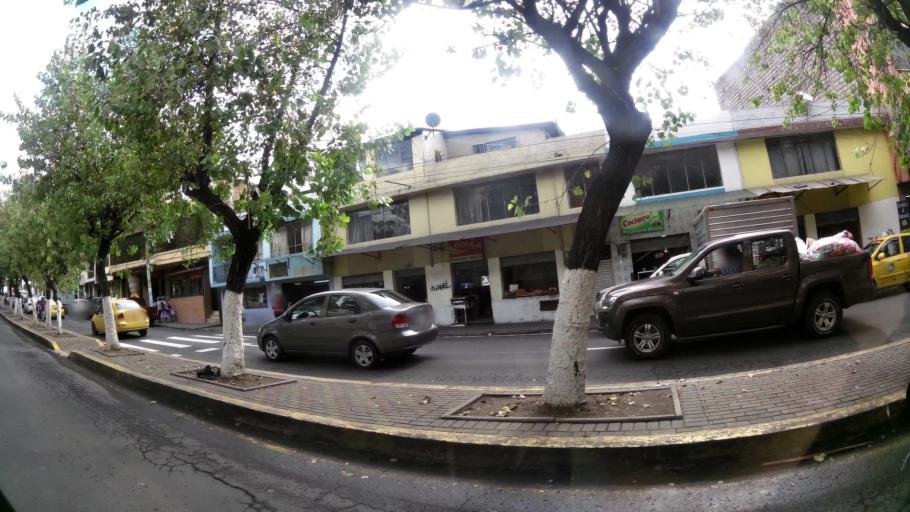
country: EC
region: Pichincha
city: Sangolqui
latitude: -0.3262
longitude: -78.4499
